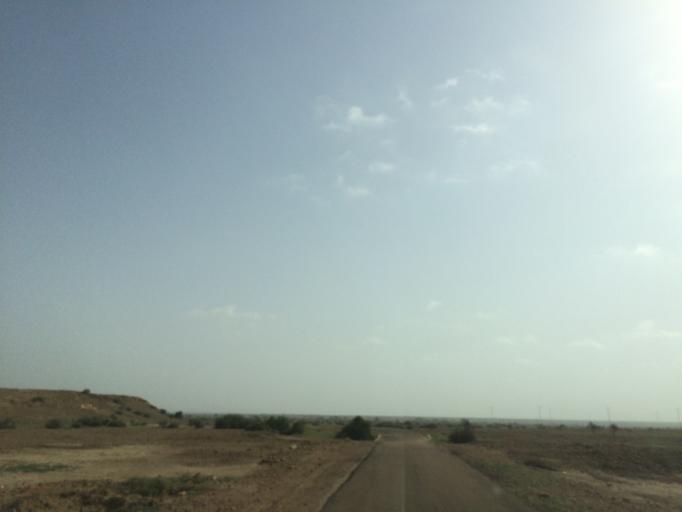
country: IN
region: Rajasthan
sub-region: Jaisalmer
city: Jaisalmer
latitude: 26.7913
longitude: 70.6885
